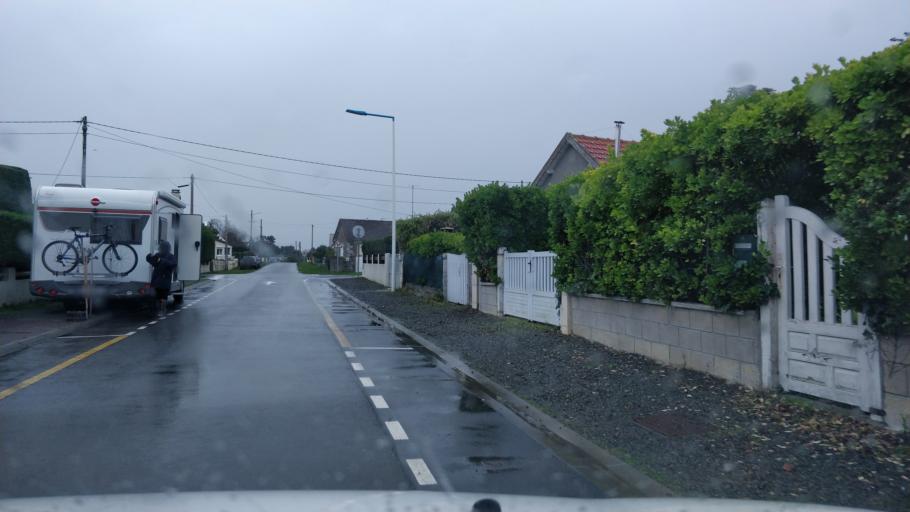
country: FR
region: Lower Normandy
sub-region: Departement de la Manche
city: Donville-les-Bains
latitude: 48.8952
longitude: -1.5686
